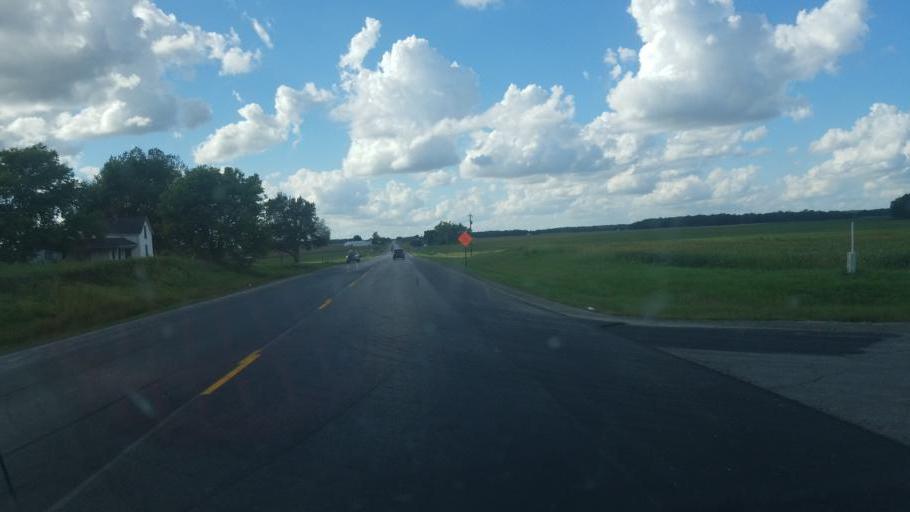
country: US
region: Ohio
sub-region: Hardin County
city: Kenton
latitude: 40.6669
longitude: -83.6549
